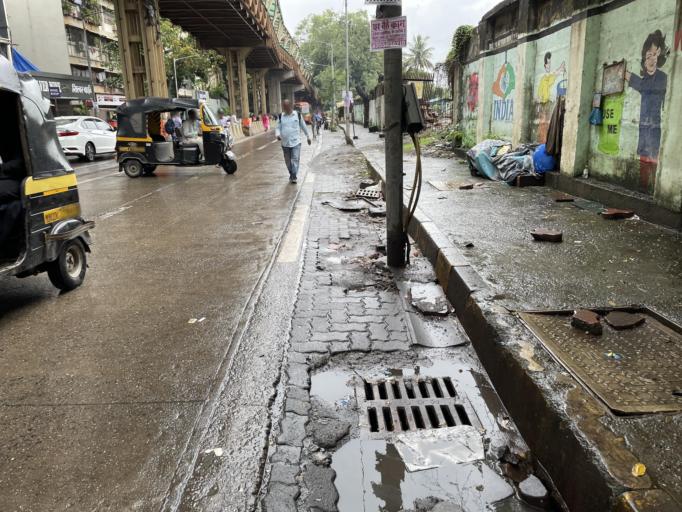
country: IN
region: Maharashtra
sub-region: Mumbai Suburban
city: Borivli
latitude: 19.2511
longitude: 72.8590
